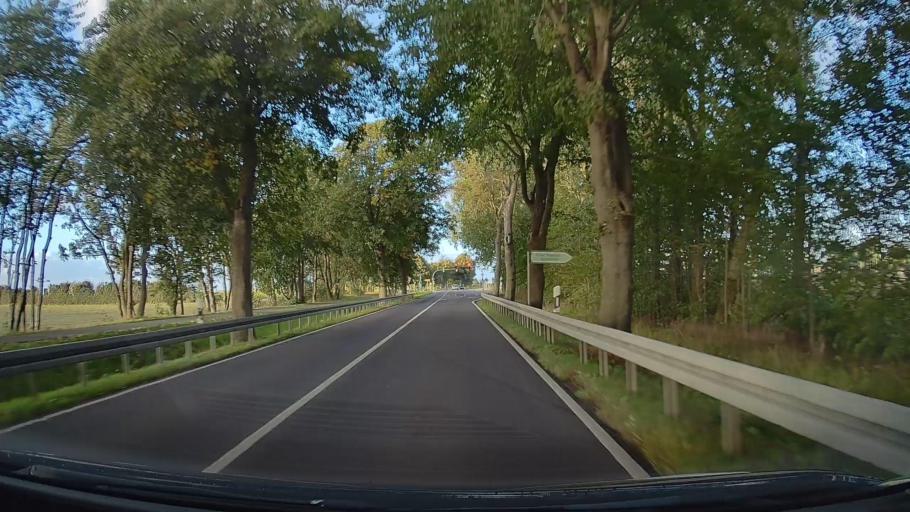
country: DE
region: Mecklenburg-Vorpommern
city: Wendorf
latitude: 54.2792
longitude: 13.0445
